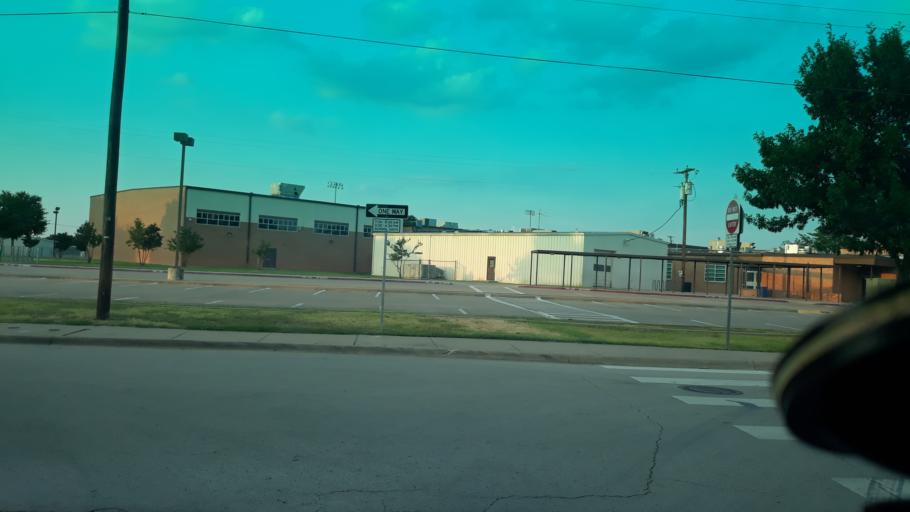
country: US
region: Texas
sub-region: Dallas County
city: Irving
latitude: 32.8345
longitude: -96.9792
